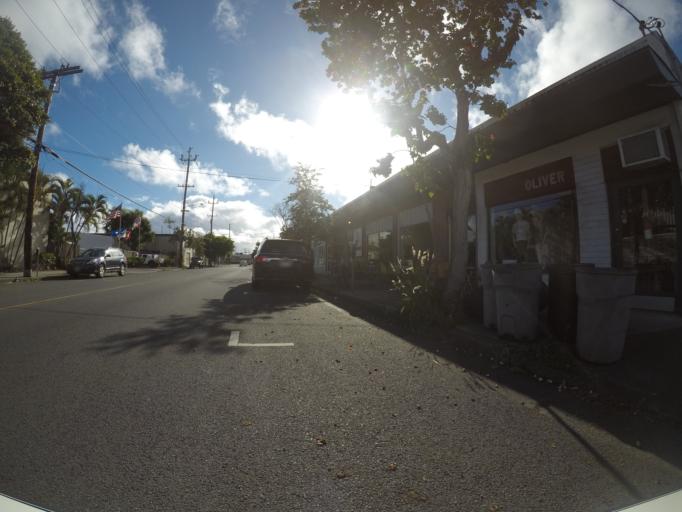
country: US
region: Hawaii
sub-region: Honolulu County
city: Kailua
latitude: 21.3949
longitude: -157.7459
